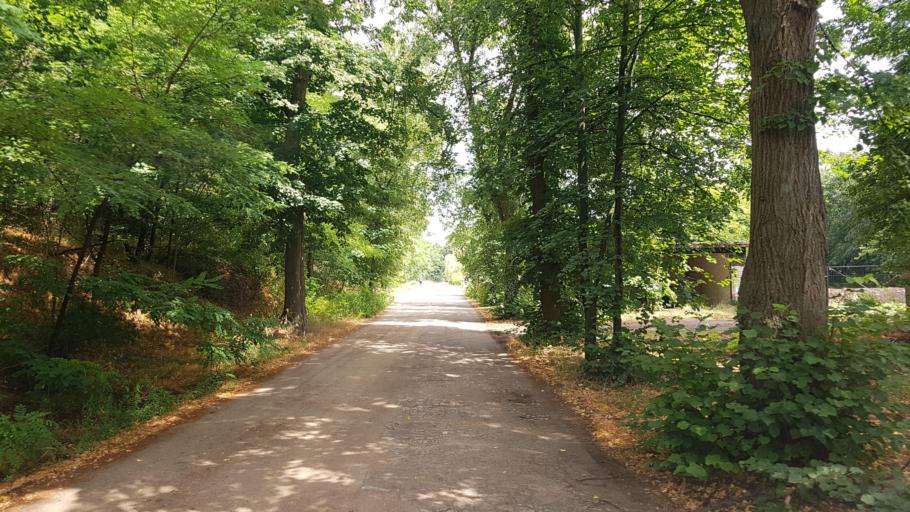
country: DE
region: Brandenburg
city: Trebbin
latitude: 52.2420
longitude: 13.1575
